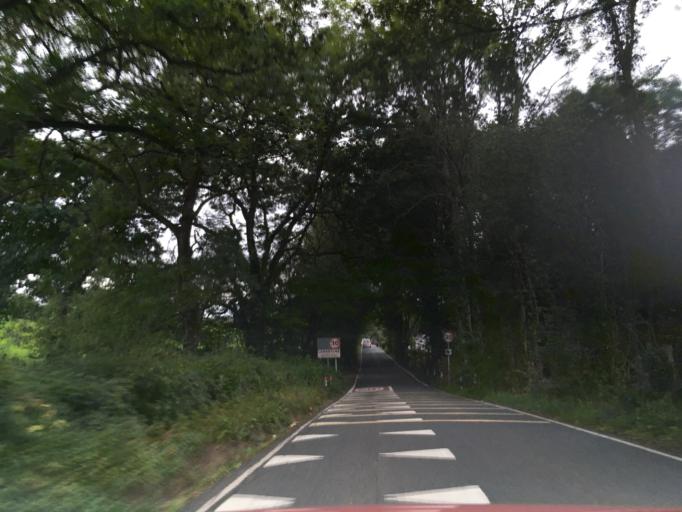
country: GB
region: Wales
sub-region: Newport
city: Langstone
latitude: 51.6085
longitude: -2.9113
